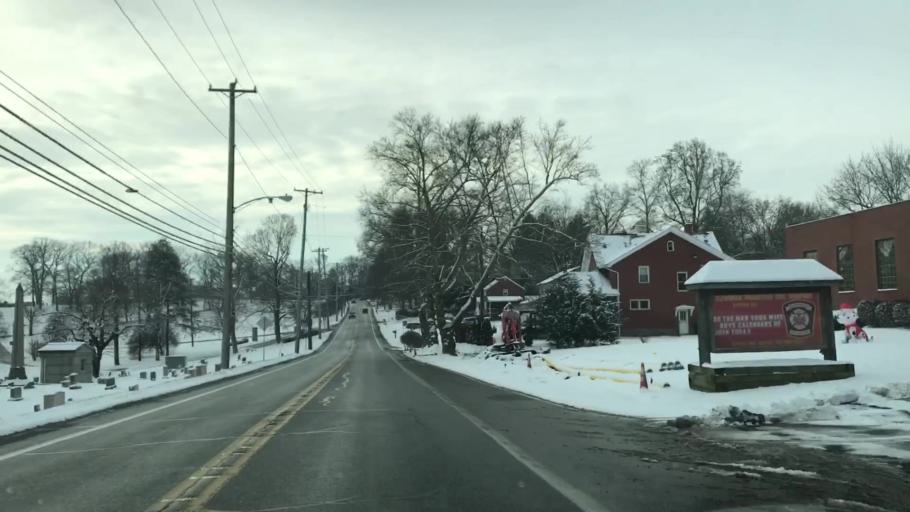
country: US
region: Pennsylvania
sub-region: Allegheny County
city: Glenshaw
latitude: 40.5421
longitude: -79.9723
